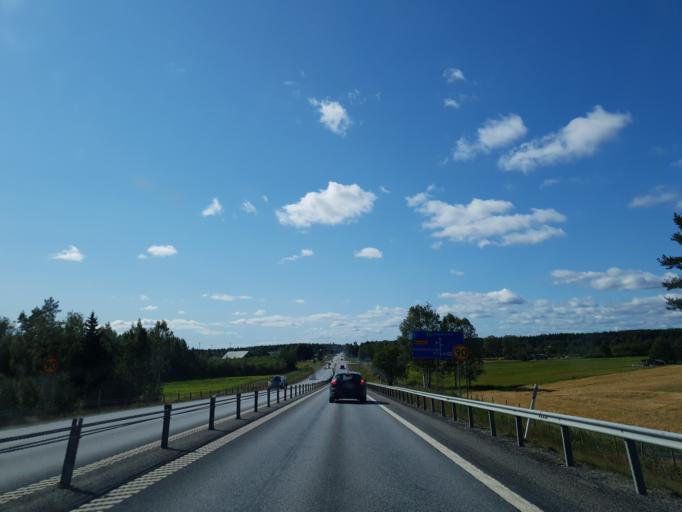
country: SE
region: Vaesterbotten
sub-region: Umea Kommun
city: Hoernefors
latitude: 63.6867
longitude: 20.0100
